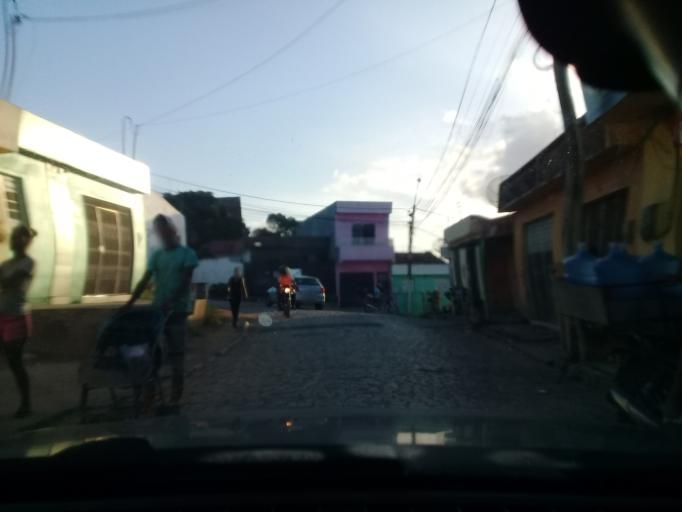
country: BR
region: Pernambuco
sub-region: Vitoria De Santo Antao
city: Vitoria de Santo Antao
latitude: -8.1272
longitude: -35.2841
